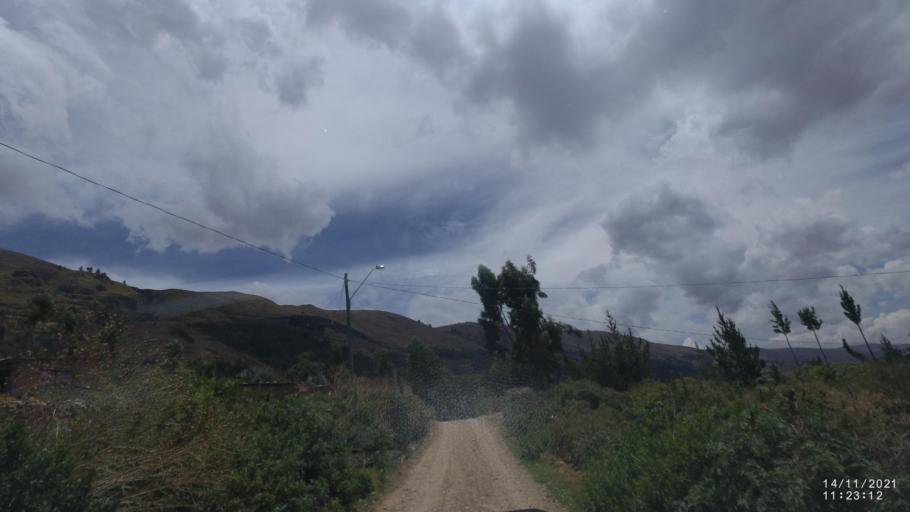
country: BO
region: Cochabamba
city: Cochabamba
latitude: -17.3353
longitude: -66.0306
